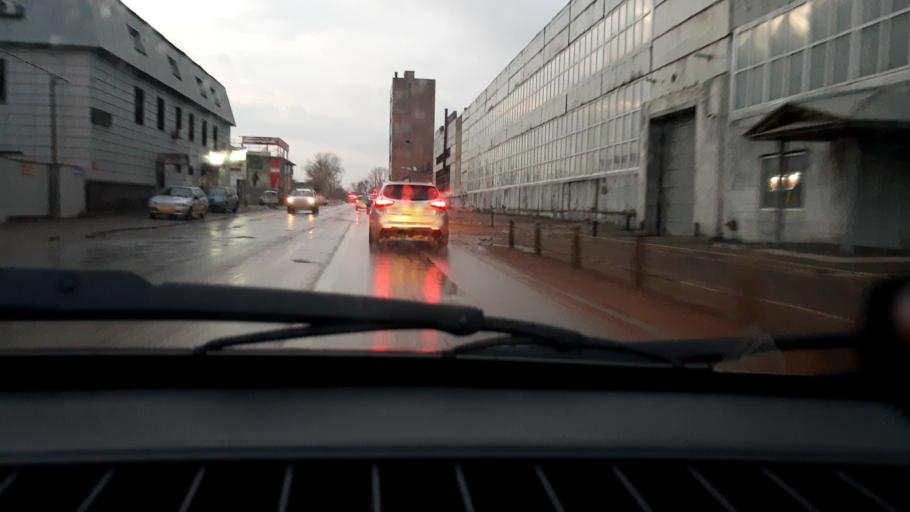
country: RU
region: Bashkortostan
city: Ufa
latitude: 54.7452
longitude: 55.9214
